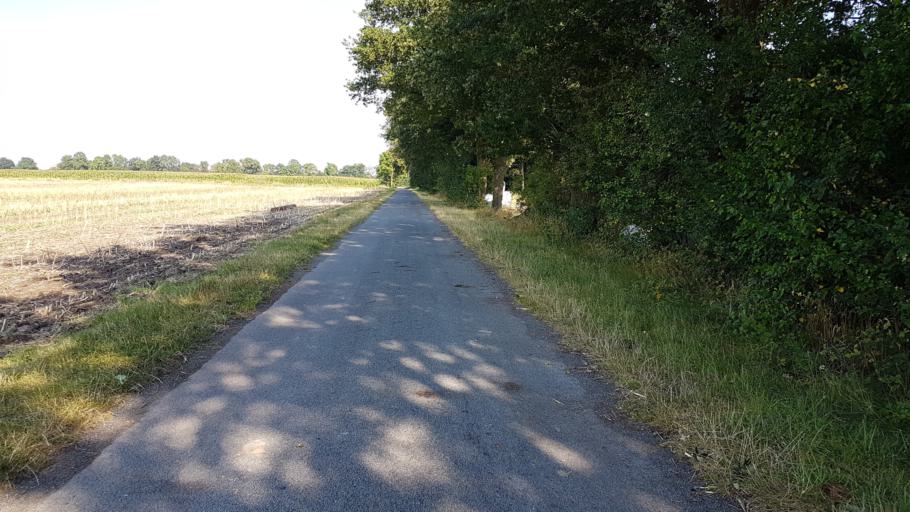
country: DE
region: North Rhine-Westphalia
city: Olfen
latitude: 51.6901
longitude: 7.3692
